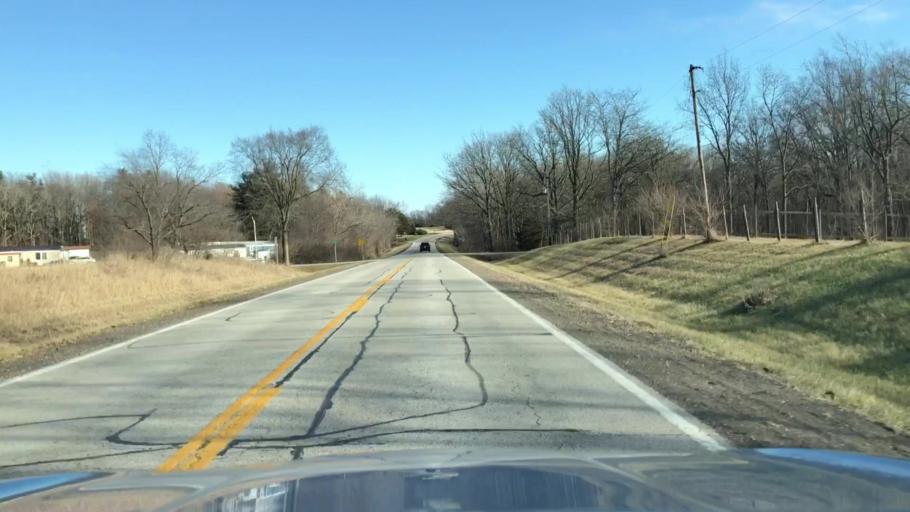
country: US
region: Illinois
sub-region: McLean County
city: Lexington
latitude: 40.6480
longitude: -88.8464
